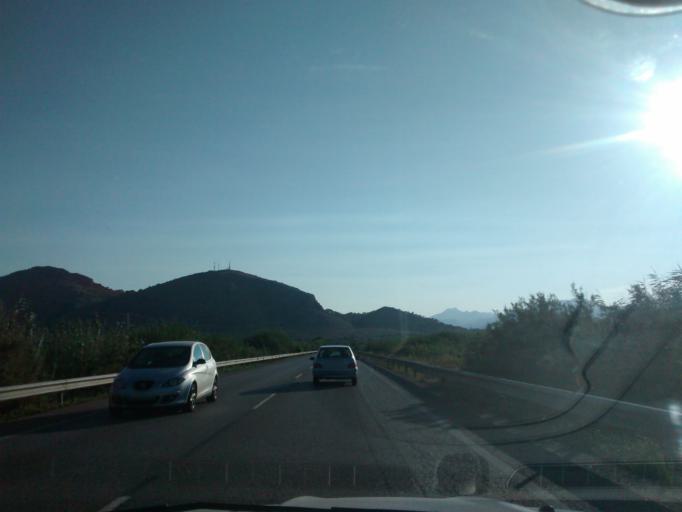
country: ES
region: Balearic Islands
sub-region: Illes Balears
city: Alcudia
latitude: 39.8446
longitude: 3.1160
